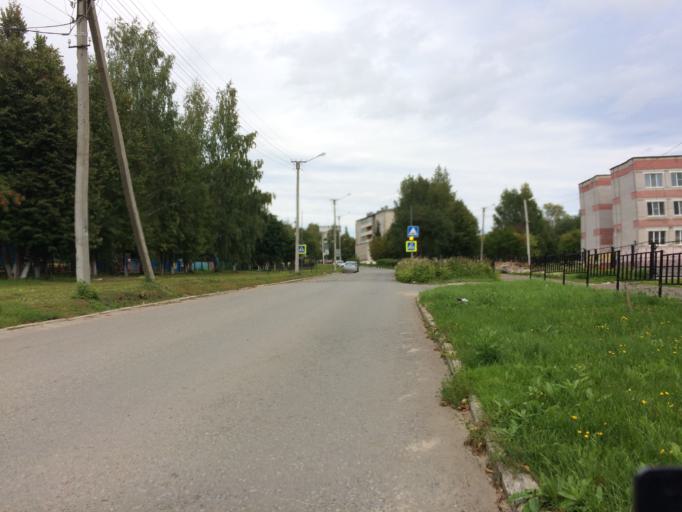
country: RU
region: Mariy-El
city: Yoshkar-Ola
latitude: 56.6490
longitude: 47.9668
